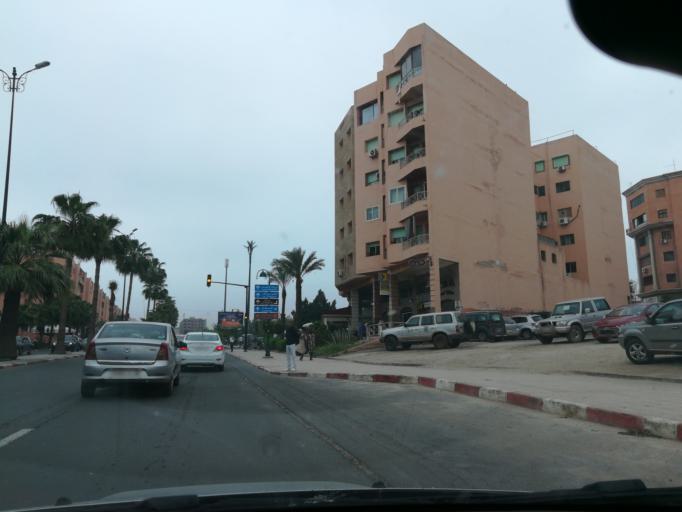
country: MA
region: Marrakech-Tensift-Al Haouz
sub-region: Marrakech
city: Marrakesh
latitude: 31.6654
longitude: -8.0099
